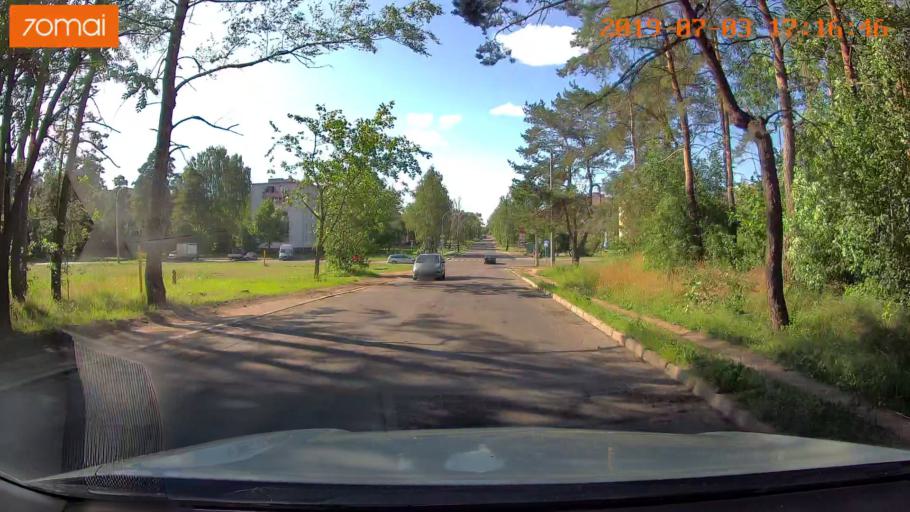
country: BY
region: Minsk
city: Vyaliki Trastsyanets
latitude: 53.9082
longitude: 27.6750
